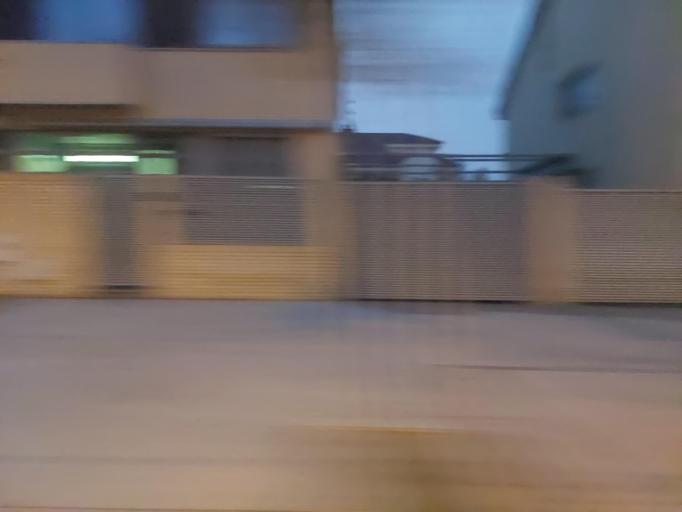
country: ES
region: Madrid
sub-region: Provincia de Madrid
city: Leganes
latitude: 40.3186
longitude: -3.7539
